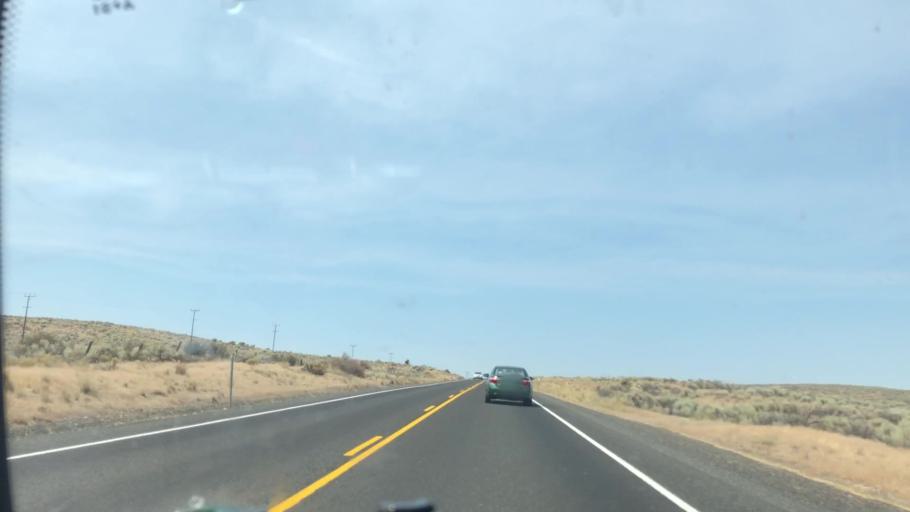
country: US
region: Idaho
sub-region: Owyhee County
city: Murphy
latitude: 42.9905
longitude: -117.0579
